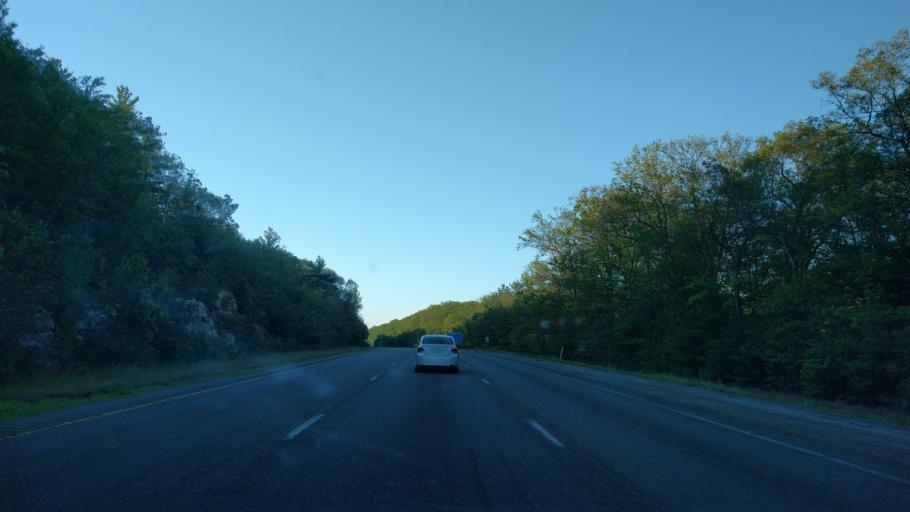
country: US
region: Massachusetts
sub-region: Middlesex County
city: Hopkinton
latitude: 42.1885
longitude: -71.5353
